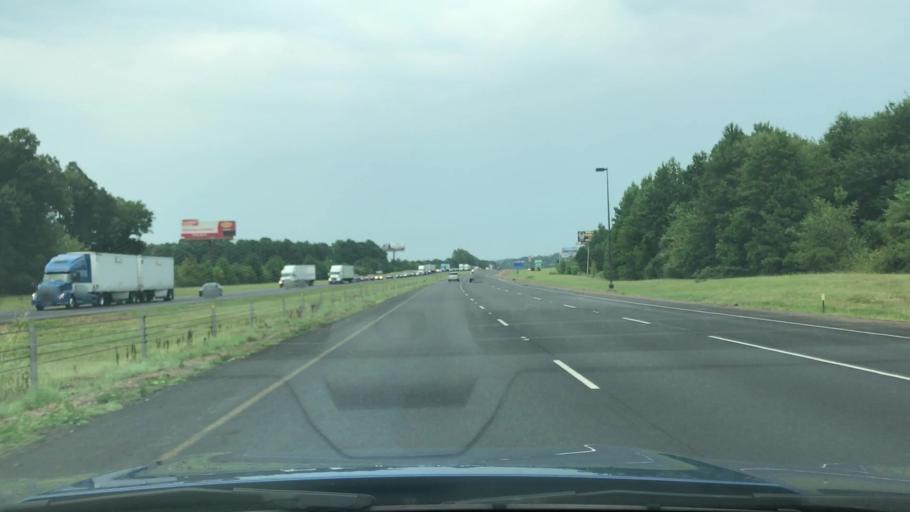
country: US
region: Louisiana
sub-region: Caddo Parish
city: Greenwood
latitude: 32.4511
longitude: -93.9961
